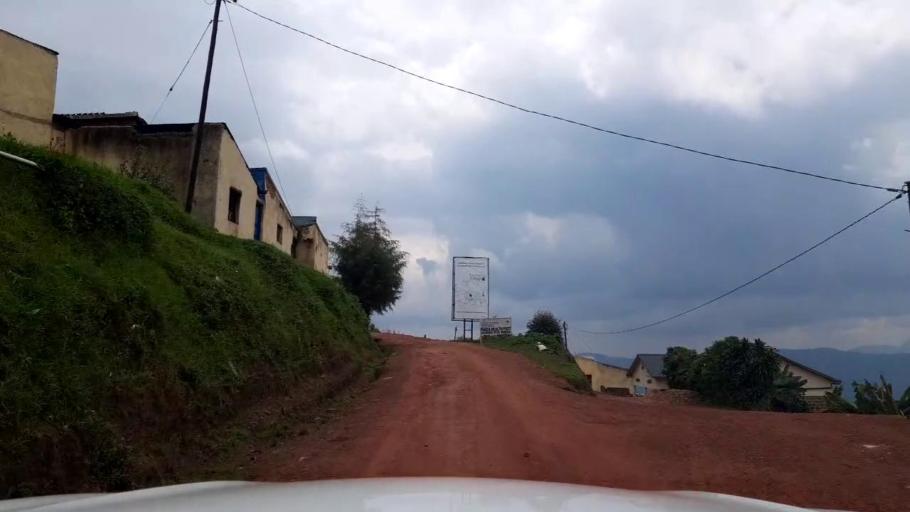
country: RW
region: Northern Province
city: Byumba
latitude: -1.5022
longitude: 29.9348
